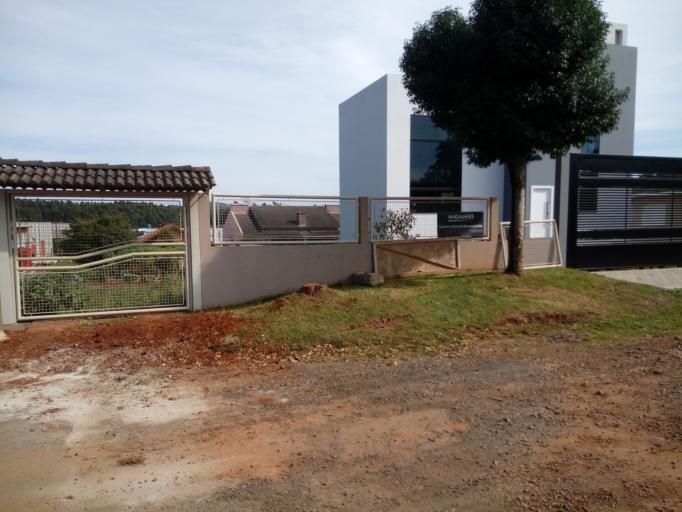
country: BR
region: Santa Catarina
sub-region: Chapeco
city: Chapeco
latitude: -27.0362
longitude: -52.6312
